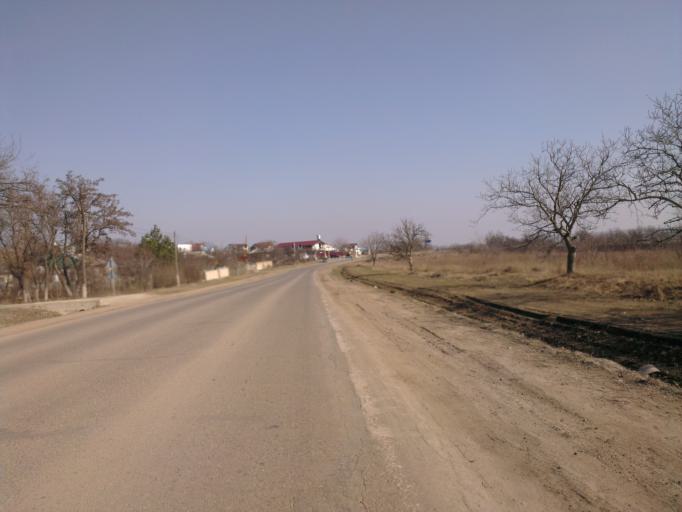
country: MD
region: Chisinau
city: Ciorescu
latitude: 47.1186
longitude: 28.8712
